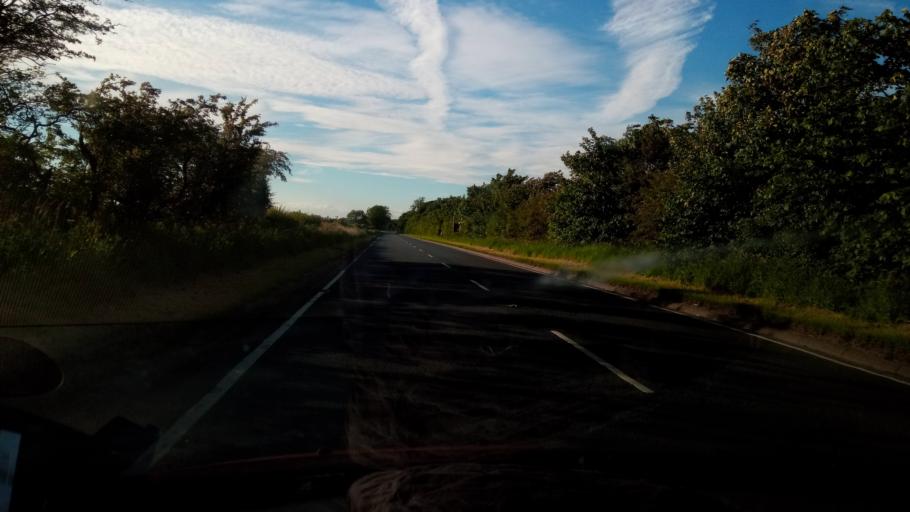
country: GB
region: England
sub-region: Cumbria
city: Carlisle
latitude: 54.9756
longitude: -2.9507
